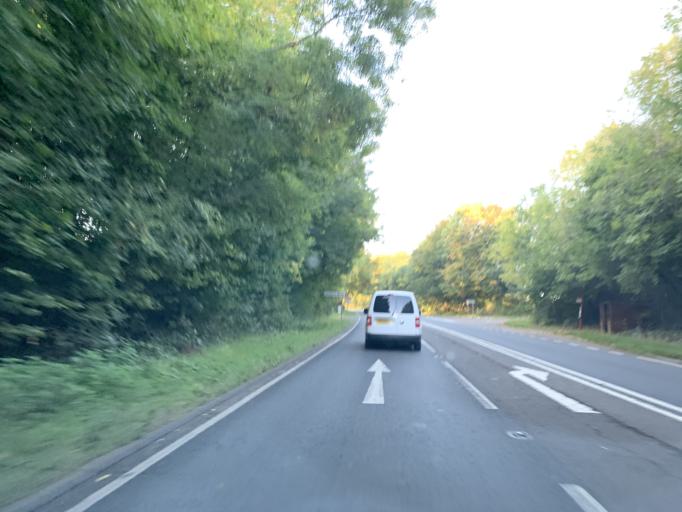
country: GB
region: England
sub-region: Wiltshire
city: Whiteparish
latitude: 50.9879
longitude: -1.6413
